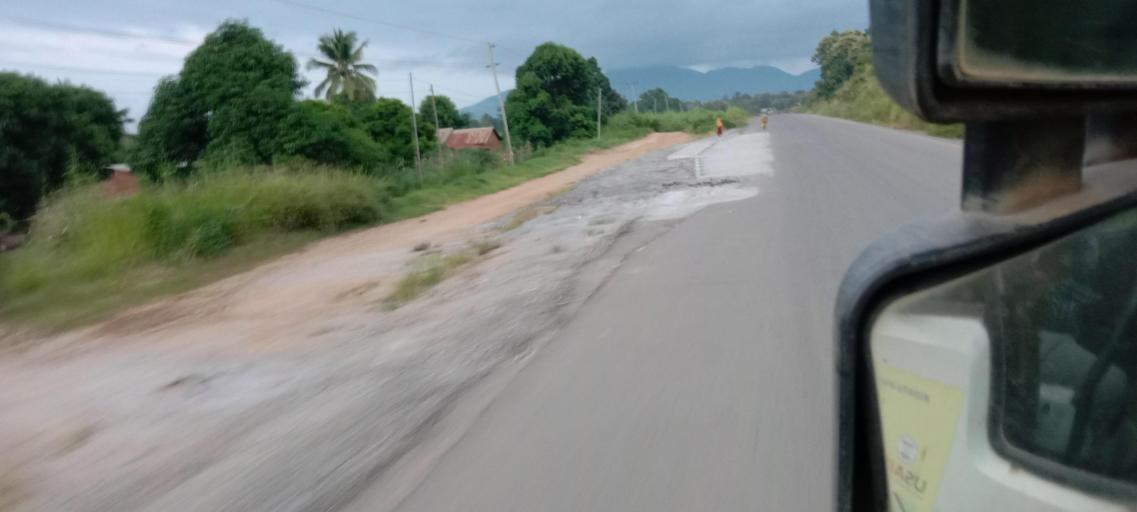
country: TZ
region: Morogoro
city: Ifakara
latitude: -7.9594
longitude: 36.8523
